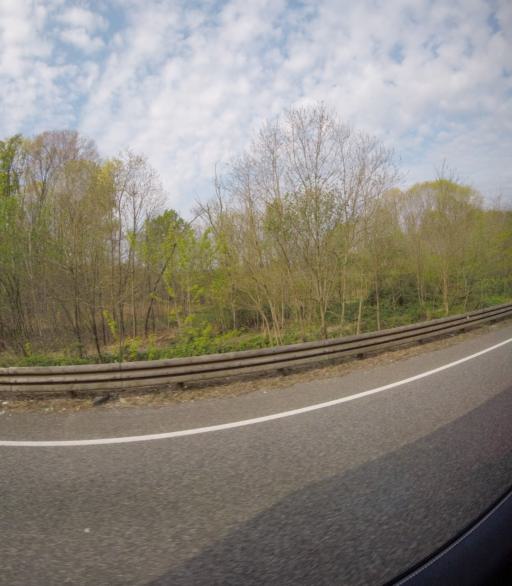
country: IT
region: Piedmont
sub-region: Provincia di Novara
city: Borgomanero
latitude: 45.7181
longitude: 8.4751
